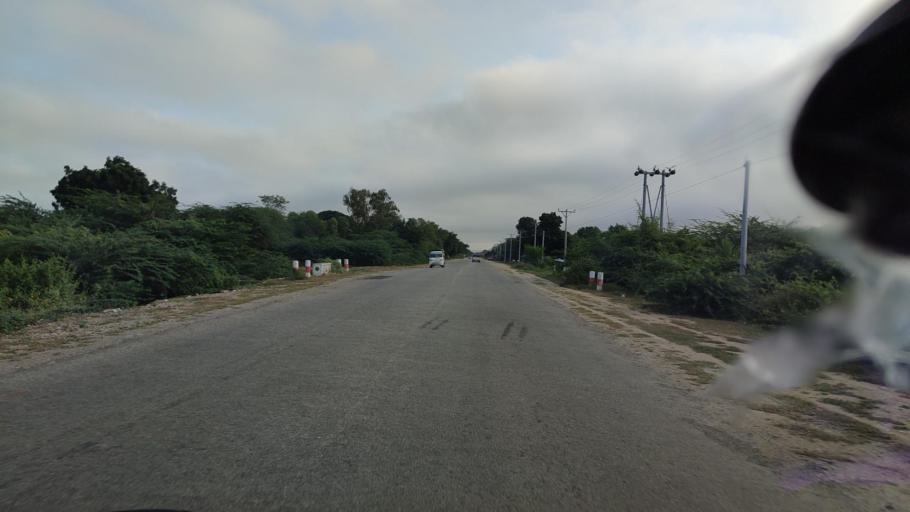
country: MM
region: Mandalay
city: Yamethin
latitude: 20.7101
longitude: 96.1812
